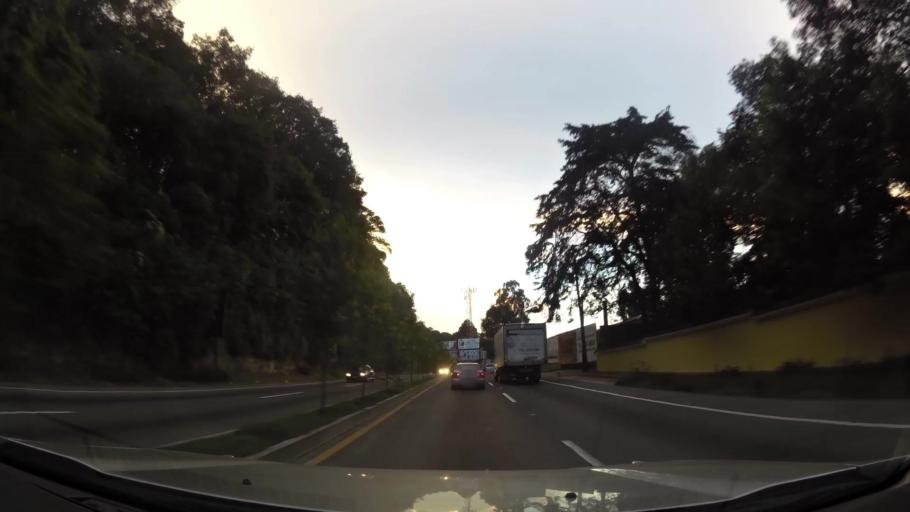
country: GT
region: Sacatepequez
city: San Lucas Sacatepequez
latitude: 14.6069
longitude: -90.6502
